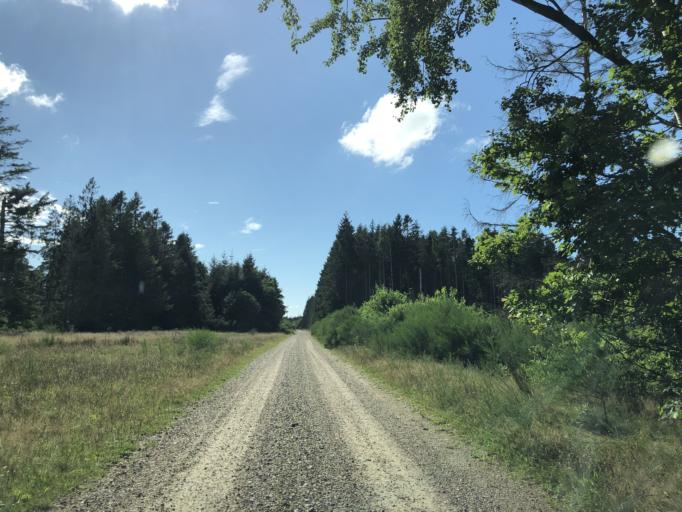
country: DK
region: Central Jutland
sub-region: Holstebro Kommune
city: Ulfborg
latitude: 56.2210
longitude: 8.4666
